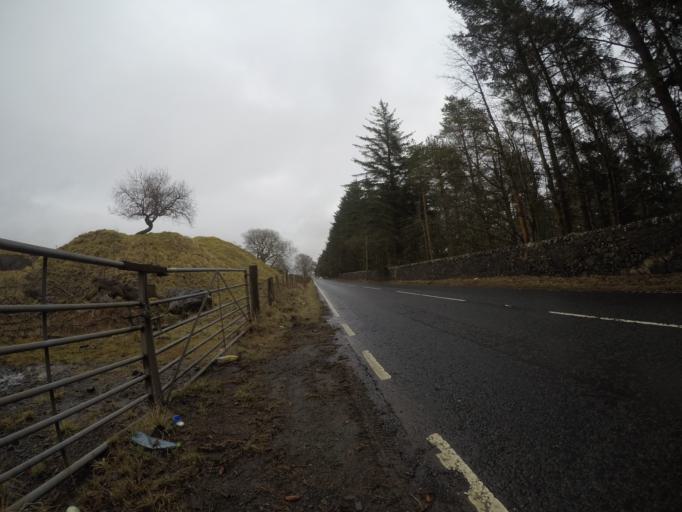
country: GB
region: Scotland
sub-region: North Ayrshire
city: Fairlie
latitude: 55.7753
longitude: -4.8298
